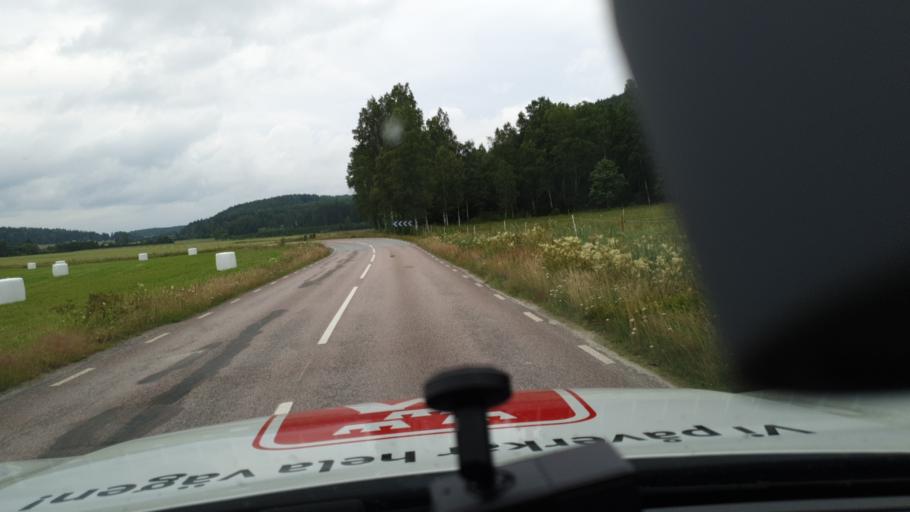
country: SE
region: Vaermland
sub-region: Sunne Kommun
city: Sunne
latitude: 59.8106
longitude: 13.2272
